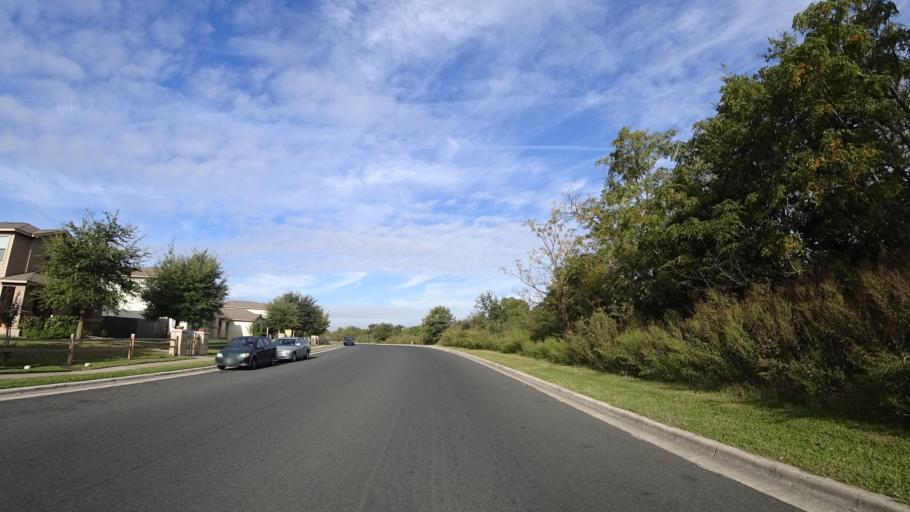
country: US
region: Texas
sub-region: Travis County
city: Austin
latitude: 30.2003
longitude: -97.7295
